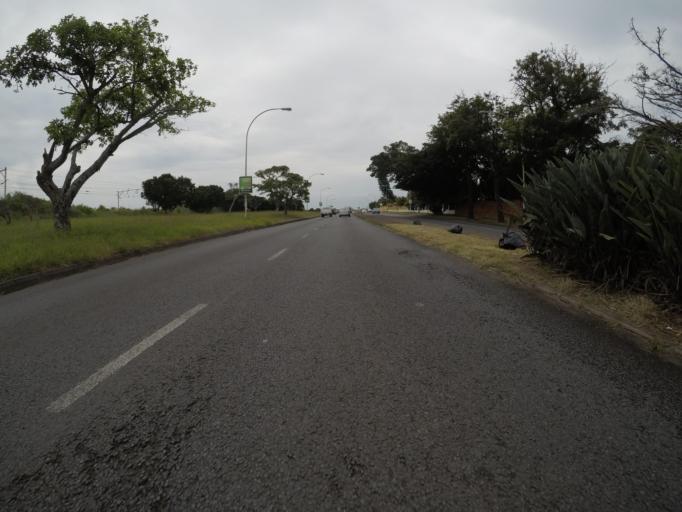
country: ZA
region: Eastern Cape
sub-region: Buffalo City Metropolitan Municipality
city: East London
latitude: -32.9861
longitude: 27.8956
